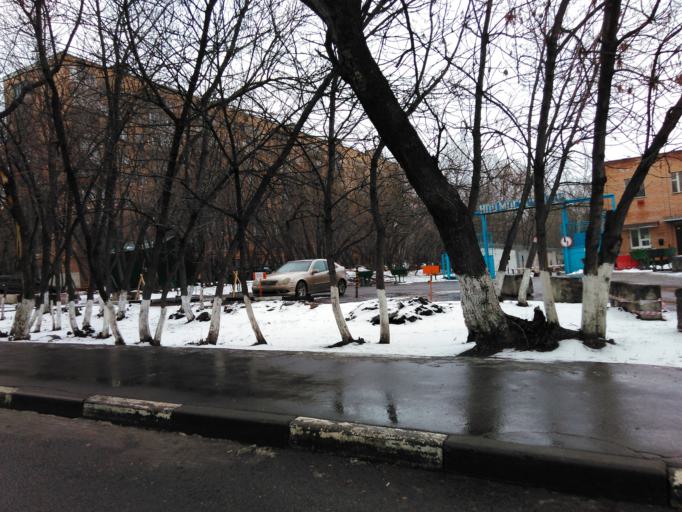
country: RU
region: Moscow
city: Nagornyy
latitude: 55.6573
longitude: 37.6240
